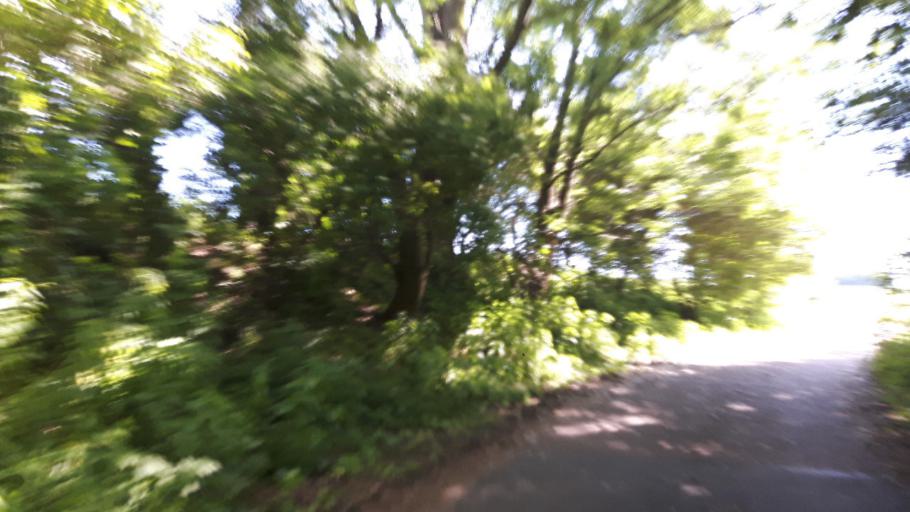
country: DE
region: Saxony-Anhalt
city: Grosskorbetha
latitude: 51.2317
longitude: 12.0375
